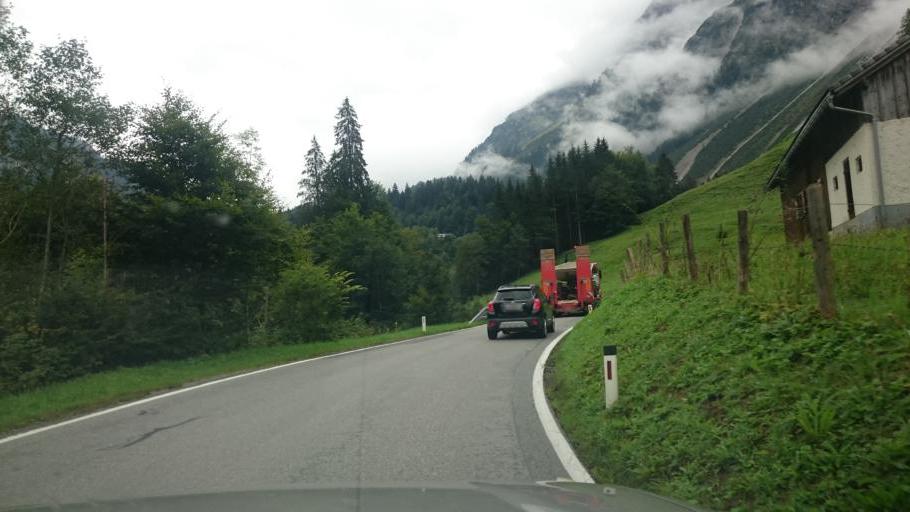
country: AT
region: Vorarlberg
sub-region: Politischer Bezirk Bregenz
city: Schoppernau
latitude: 47.2935
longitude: 10.0450
